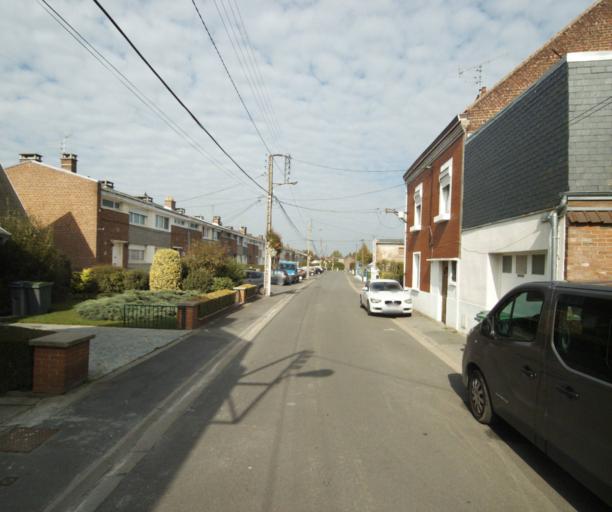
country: FR
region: Nord-Pas-de-Calais
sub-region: Departement du Nord
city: Wattignies
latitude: 50.5808
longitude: 3.0319
